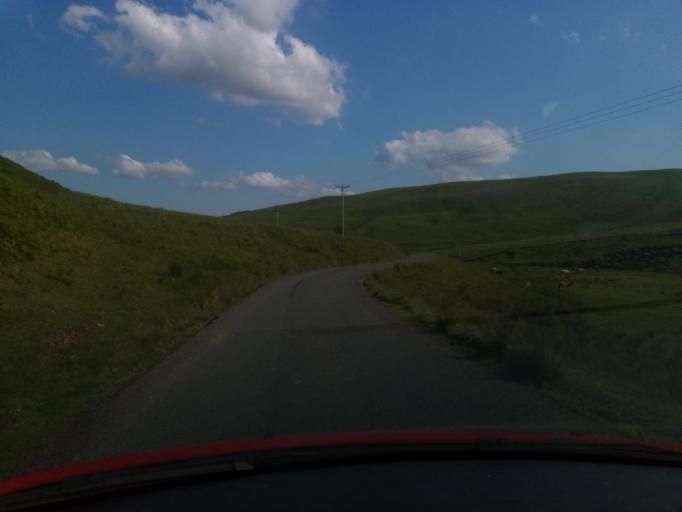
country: GB
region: Scotland
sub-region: The Scottish Borders
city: Innerleithen
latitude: 55.4593
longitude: -3.1143
